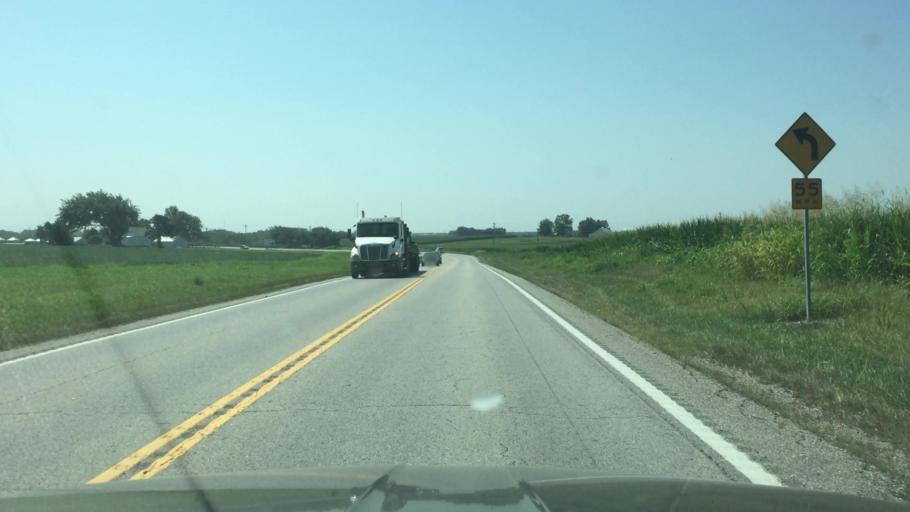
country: US
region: Missouri
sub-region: Moniteau County
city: Tipton
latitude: 38.6571
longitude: -92.8071
